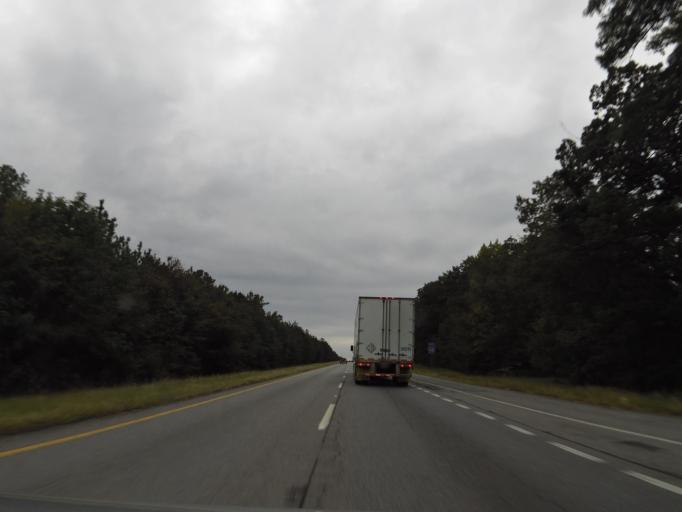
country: US
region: Alabama
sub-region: Saint Clair County
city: Steele
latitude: 33.9302
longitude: -86.1988
